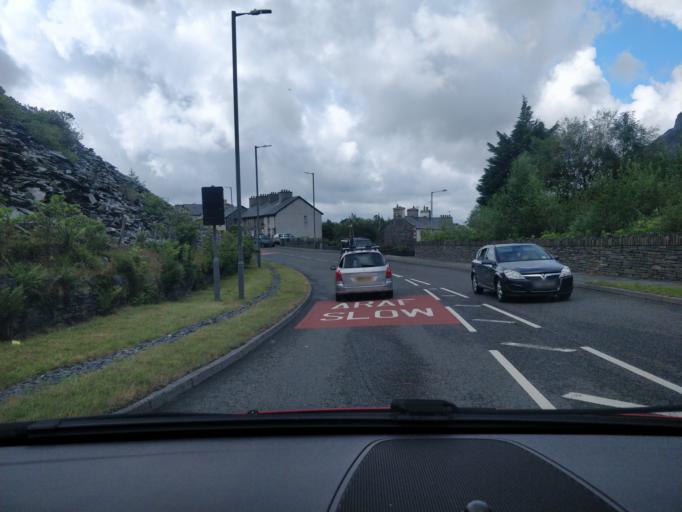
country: GB
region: Wales
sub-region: Gwynedd
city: Blaenau-Ffestiniog
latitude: 53.0010
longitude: -3.9427
